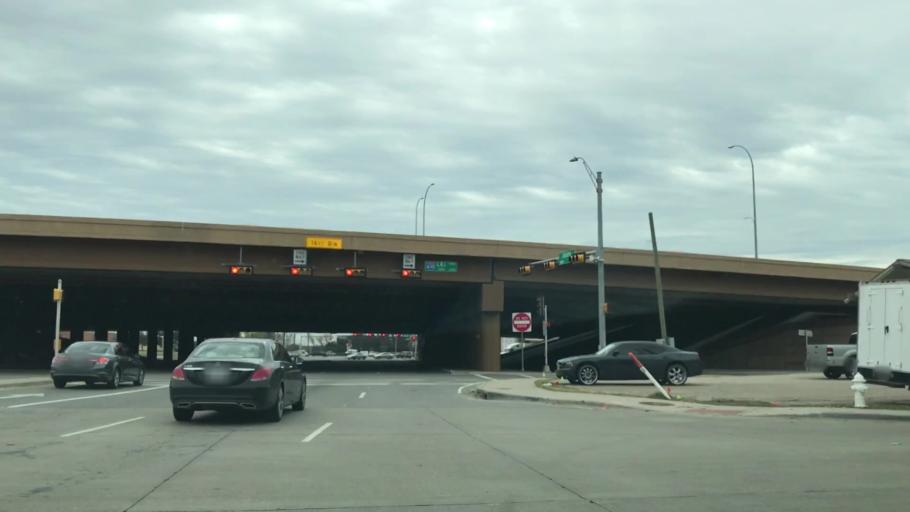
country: US
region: Texas
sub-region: Dallas County
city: Farmers Branch
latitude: 32.9121
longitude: -96.8819
